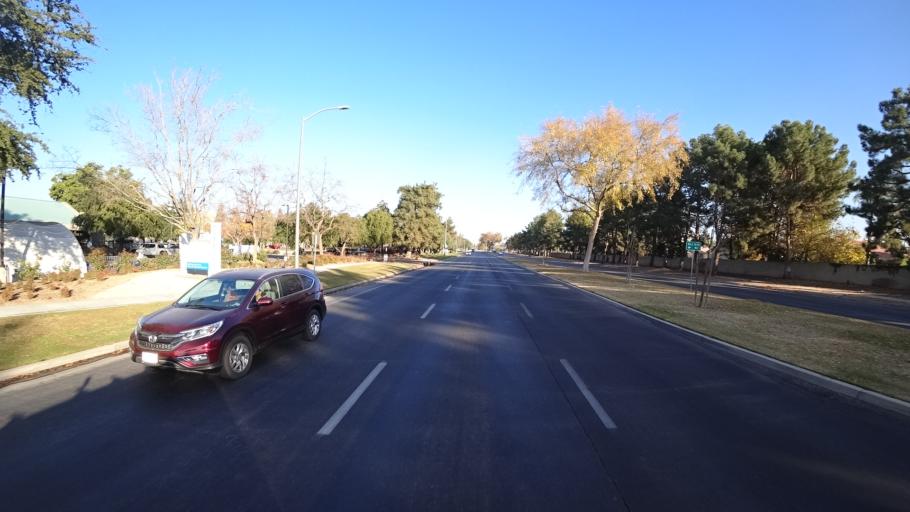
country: US
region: California
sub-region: Kern County
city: Greenacres
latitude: 35.3399
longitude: -119.0999
